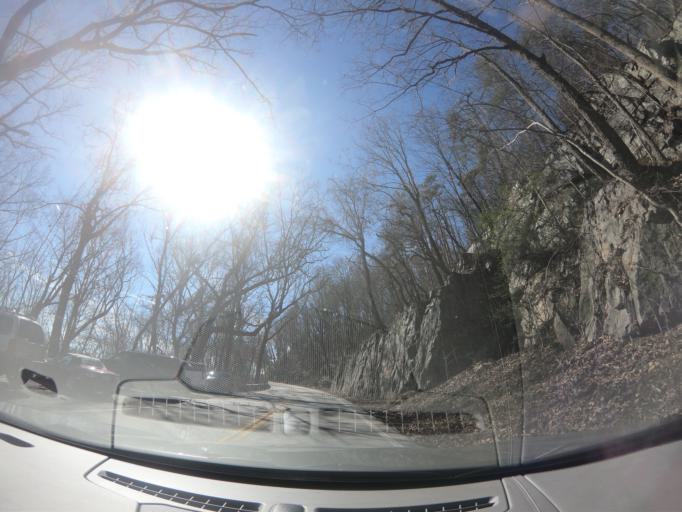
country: US
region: Tennessee
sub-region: Hamilton County
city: Lookout Mountain
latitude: 34.9923
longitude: -85.3409
